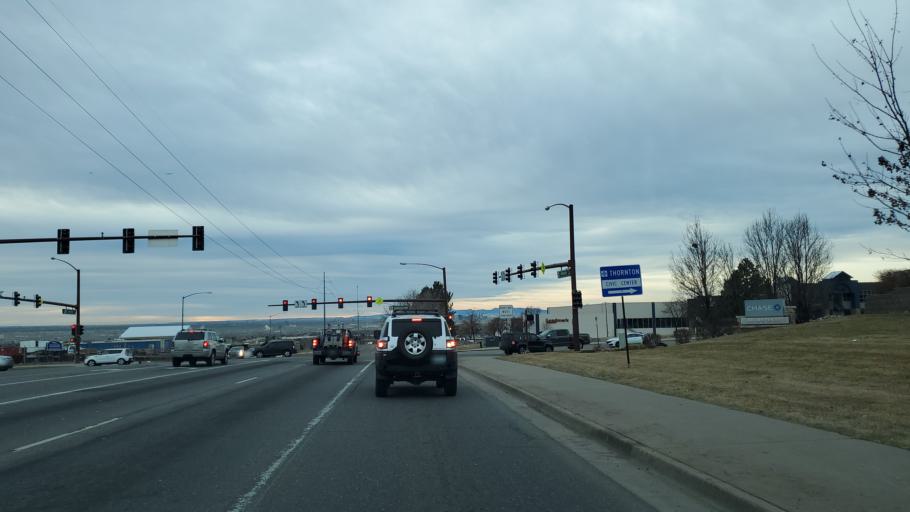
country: US
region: Colorado
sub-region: Adams County
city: Thornton
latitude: 39.8713
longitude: -104.9779
